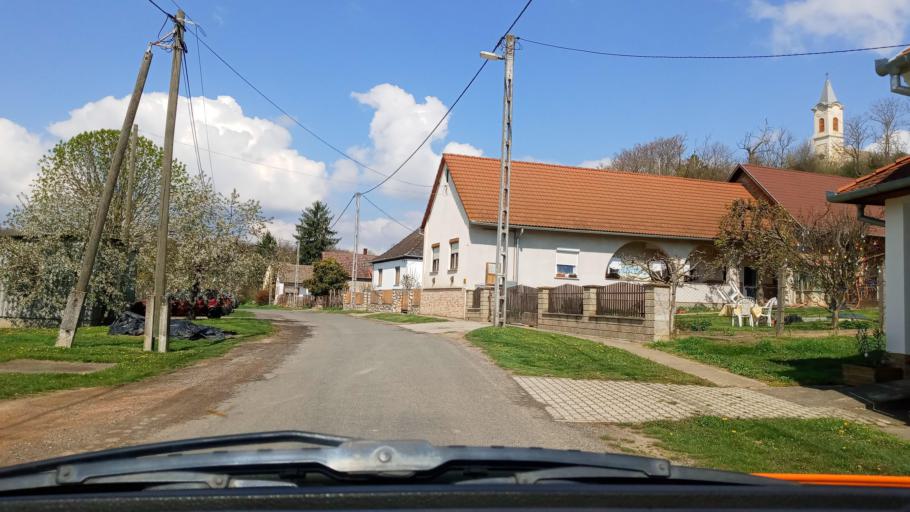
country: HU
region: Baranya
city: Boly
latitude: 46.0752
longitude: 18.5119
